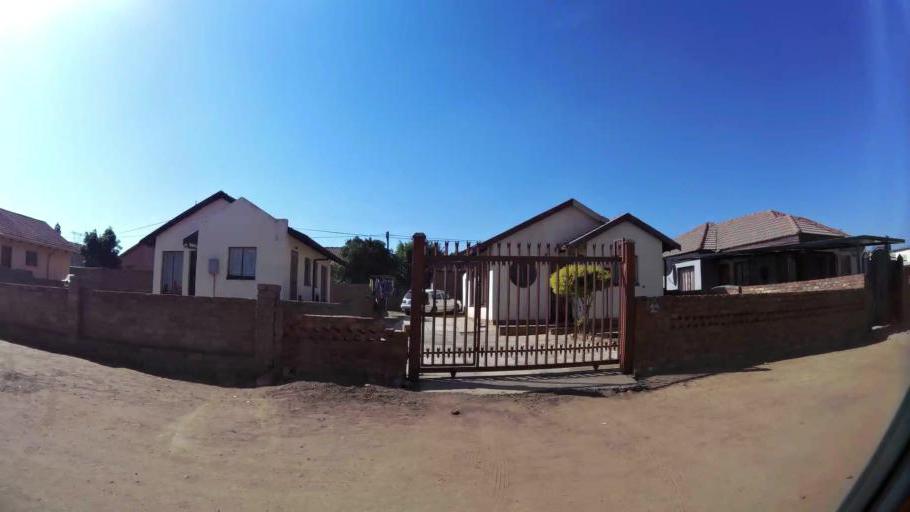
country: ZA
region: Gauteng
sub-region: City of Tshwane Metropolitan Municipality
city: Mabopane
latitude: -25.5603
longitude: 28.0823
